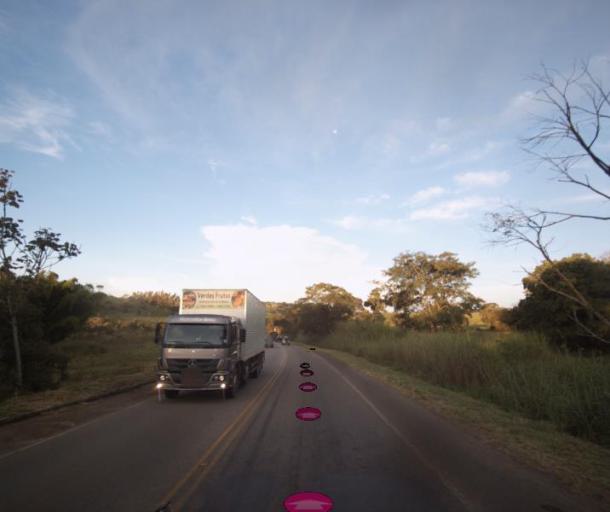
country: BR
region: Goias
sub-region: Abadiania
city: Abadiania
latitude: -16.1104
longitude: -48.8792
